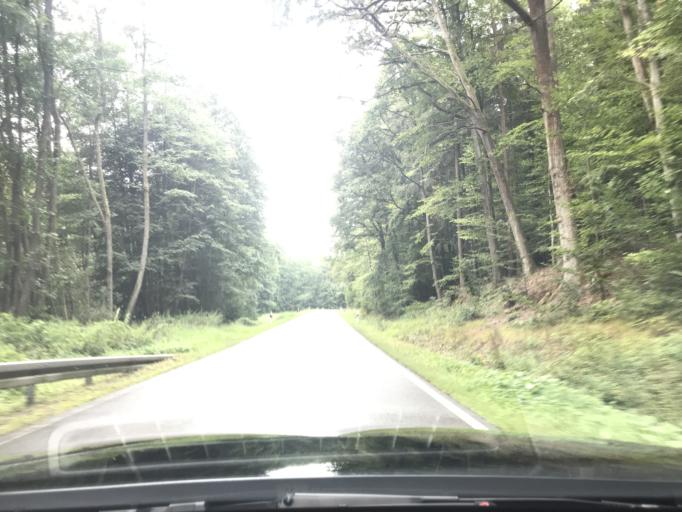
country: DE
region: Bavaria
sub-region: Regierungsbezirk Unterfranken
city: Breitbrunn
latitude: 50.0361
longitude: 10.6687
